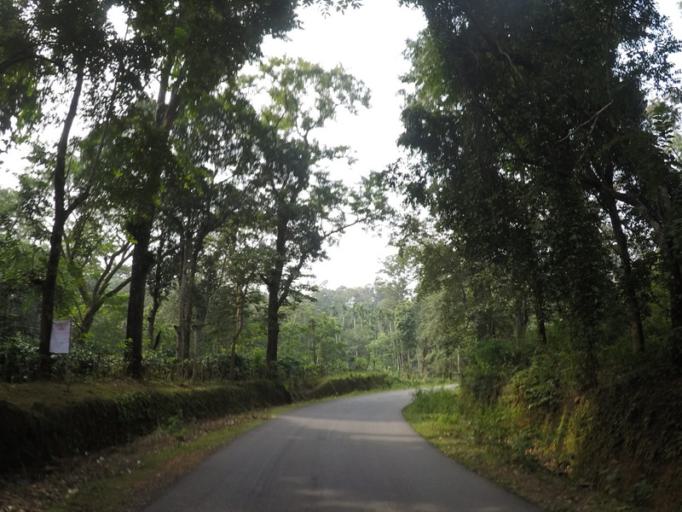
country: IN
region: Karnataka
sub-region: Chikmagalur
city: Mudigere
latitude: 13.3154
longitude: 75.4903
